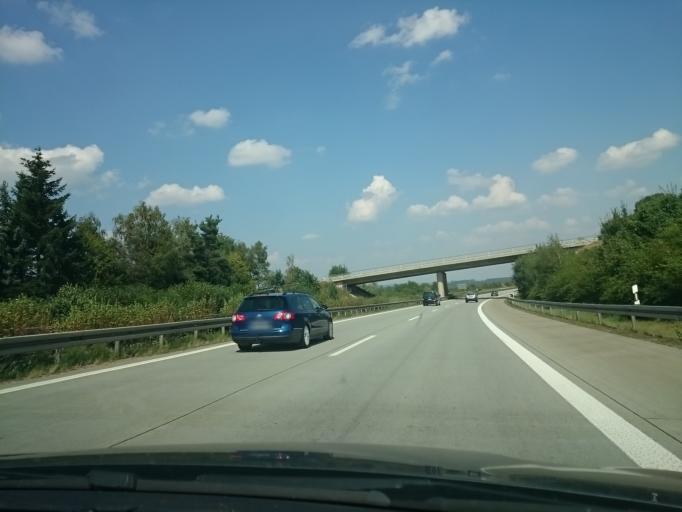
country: DE
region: Saxony
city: Stollberg
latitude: 50.7120
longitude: 12.7584
